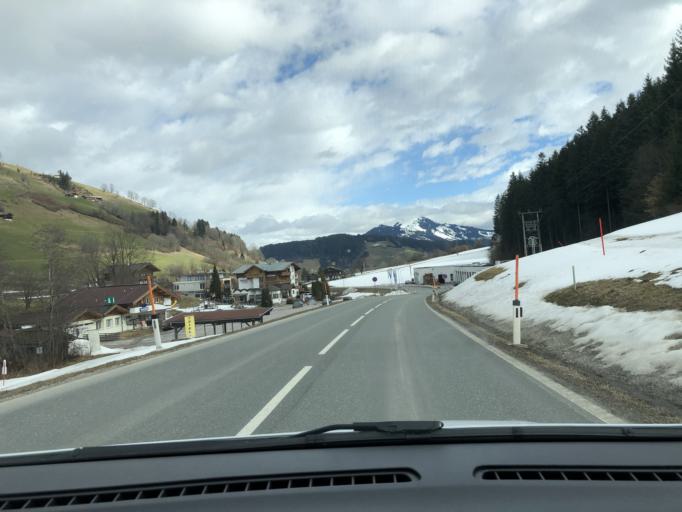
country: AT
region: Tyrol
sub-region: Politischer Bezirk Kufstein
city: Worgl
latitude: 47.4478
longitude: 12.0648
